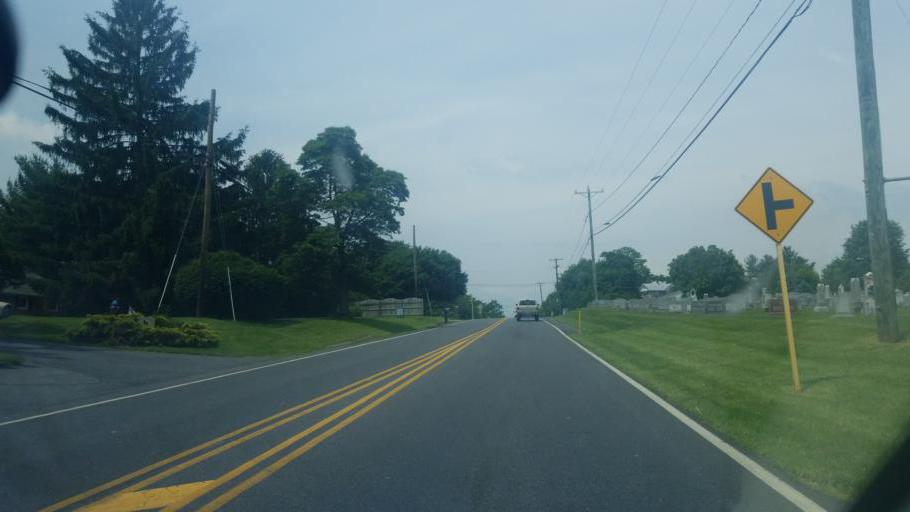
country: US
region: Virginia
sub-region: City of Harrisonburg
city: Harrisonburg
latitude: 38.4556
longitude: -78.9069
